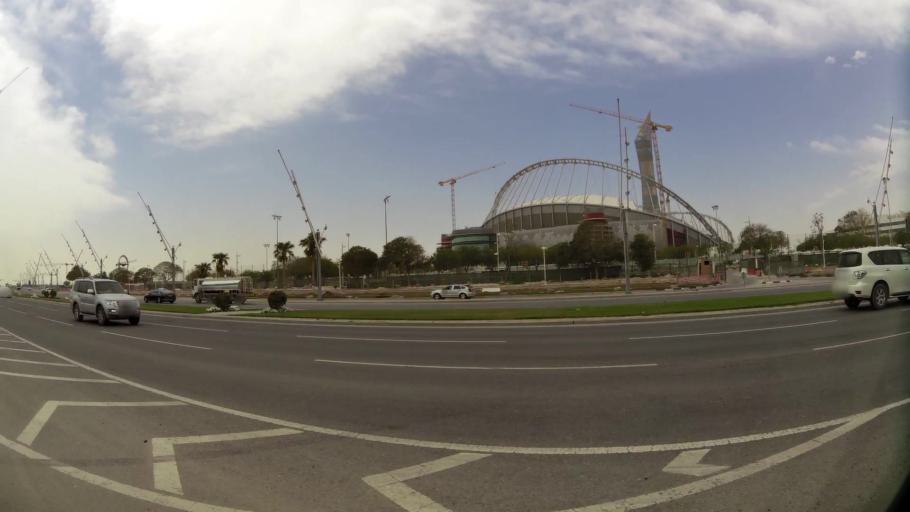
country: QA
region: Baladiyat ar Rayyan
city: Ar Rayyan
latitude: 25.2659
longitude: 51.4520
